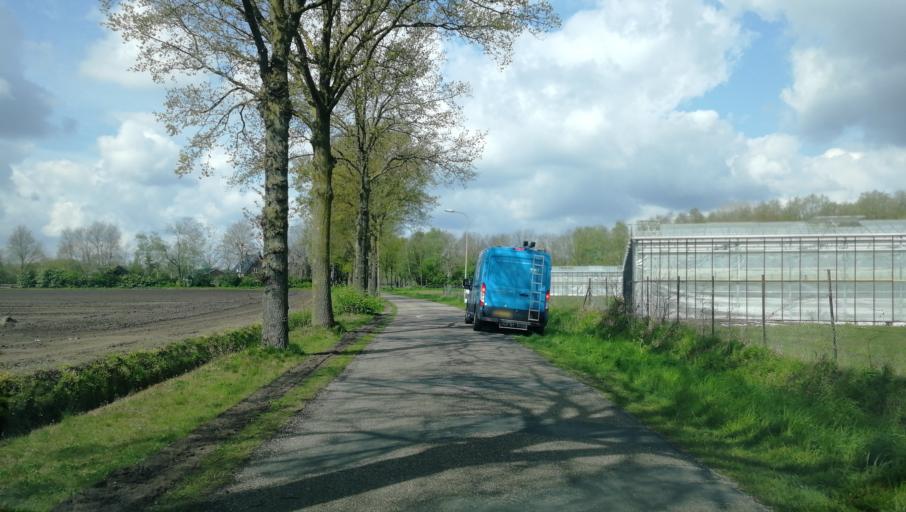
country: NL
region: Limburg
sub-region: Gemeente Peel en Maas
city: Maasbree
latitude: 51.3727
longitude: 6.0189
